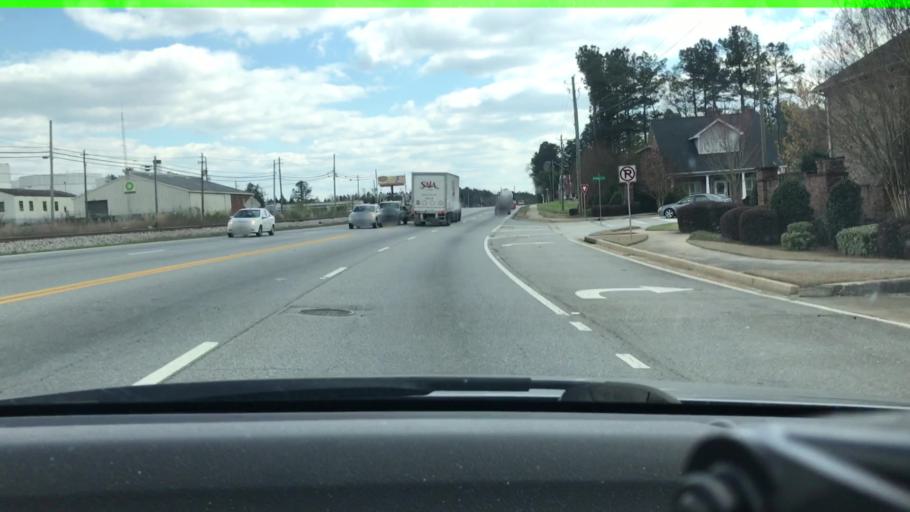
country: US
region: Georgia
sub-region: Clarke County
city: Country Club Estates
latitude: 33.9878
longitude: -83.4221
